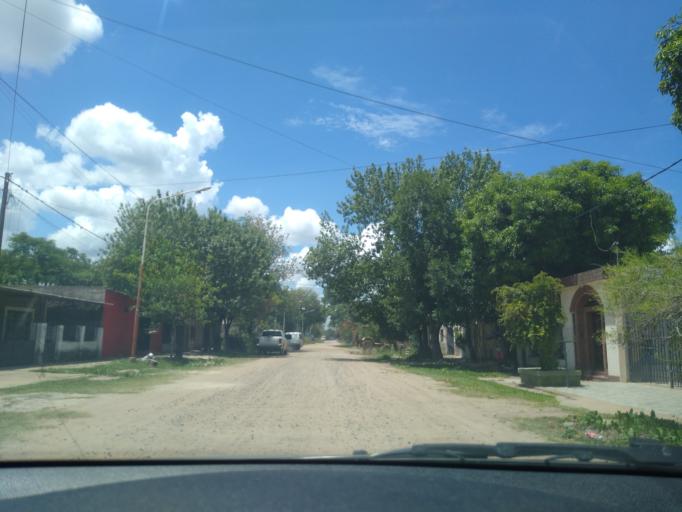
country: AR
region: Chaco
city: Barranqueras
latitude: -27.4779
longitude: -58.9358
